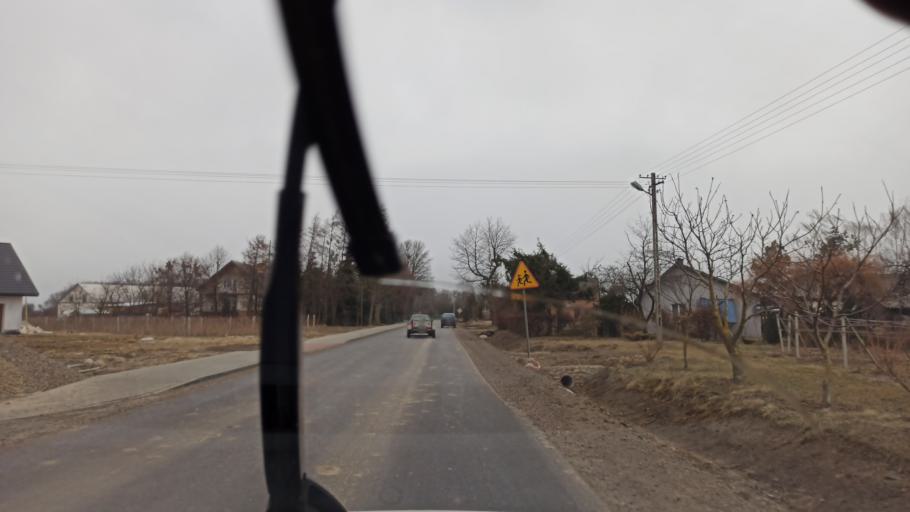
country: PL
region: Lublin Voivodeship
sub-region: Powiat lubelski
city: Bychawa
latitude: 50.9750
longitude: 22.5868
